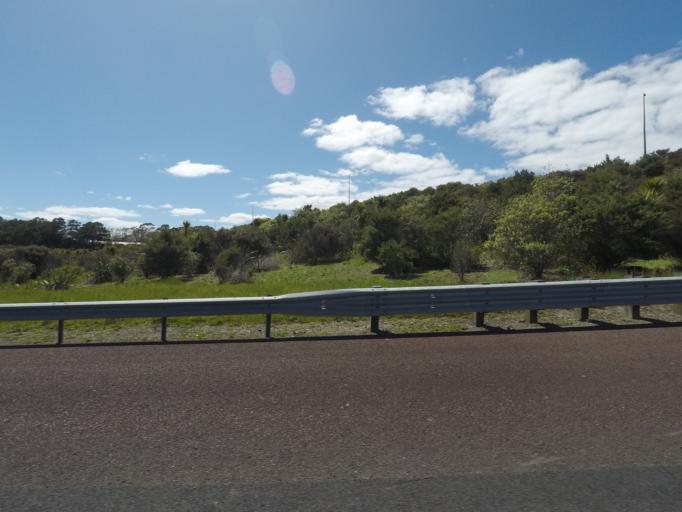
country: NZ
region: Auckland
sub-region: Auckland
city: Rosebank
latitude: -36.8135
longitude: 174.6123
